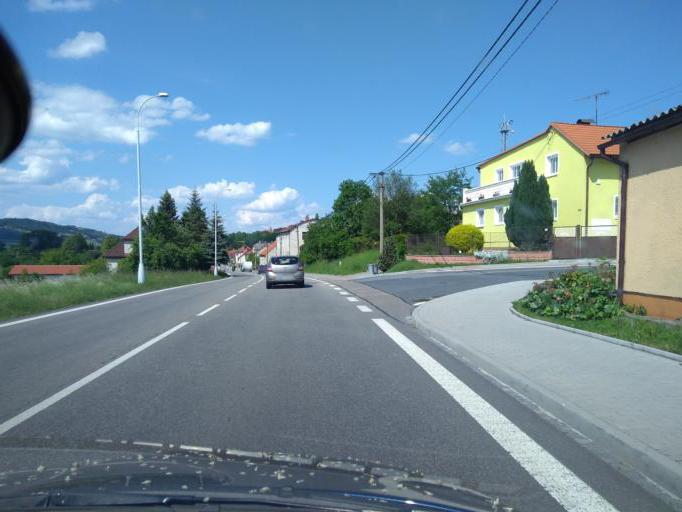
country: CZ
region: Plzensky
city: Svihov
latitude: 49.4743
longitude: 13.2902
